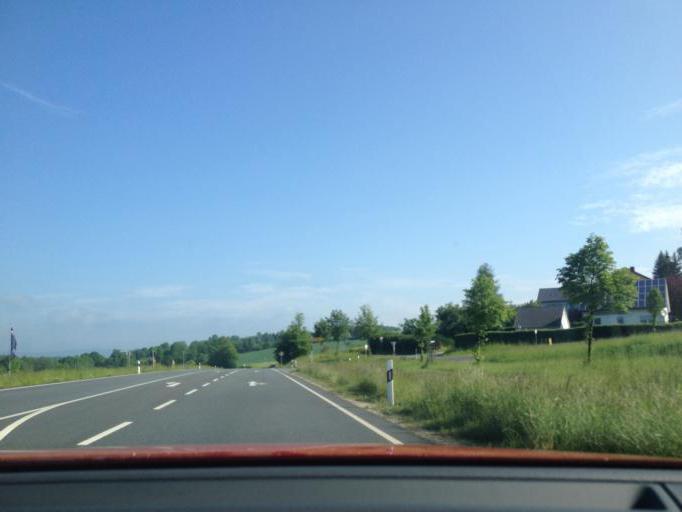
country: DE
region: Bavaria
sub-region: Upper Palatinate
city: Kastl
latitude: 49.8331
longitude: 11.8929
